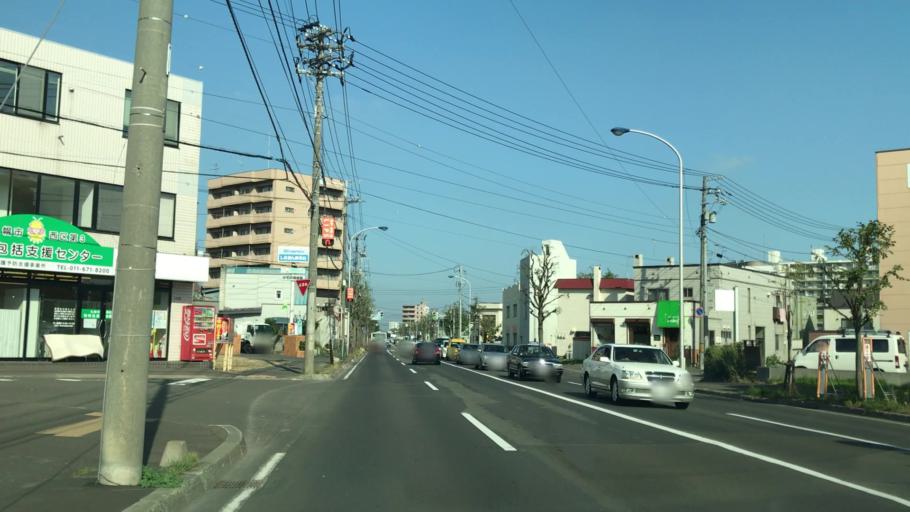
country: JP
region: Hokkaido
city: Sapporo
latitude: 43.0835
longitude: 141.3005
